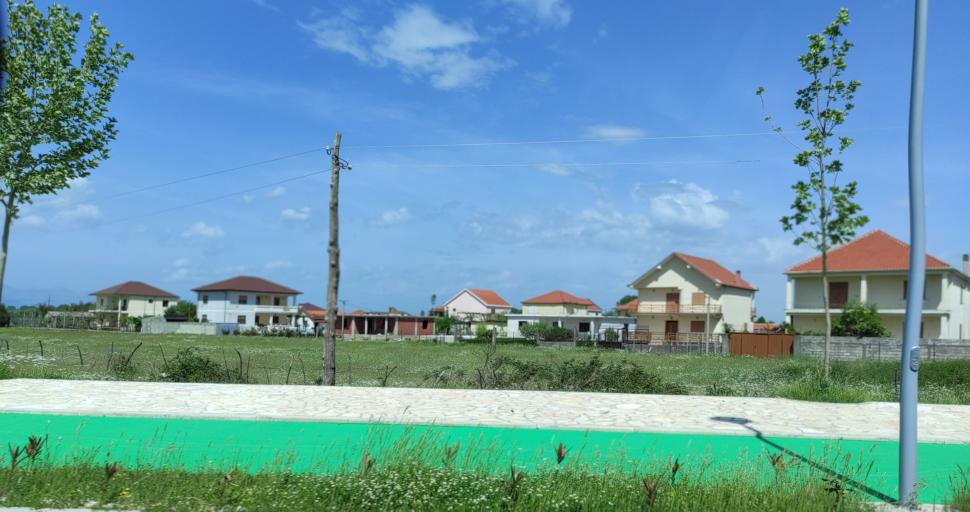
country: AL
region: Shkoder
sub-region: Rrethi i Shkodres
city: Shkoder
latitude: 42.0849
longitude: 19.5027
